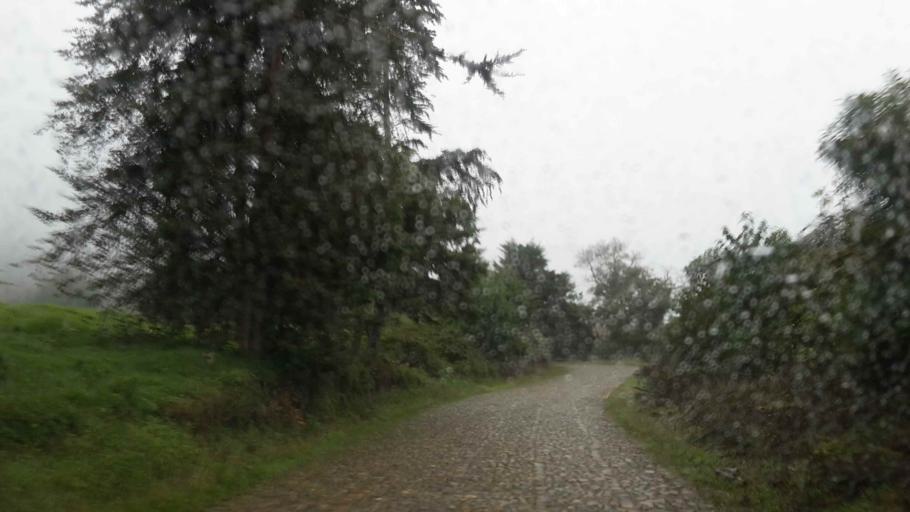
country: BO
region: Cochabamba
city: Colomi
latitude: -17.1481
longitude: -65.9141
